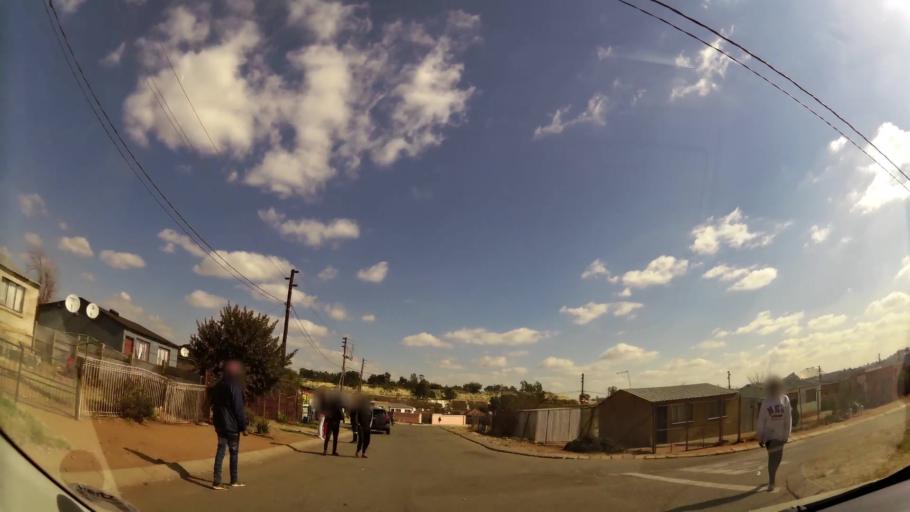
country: ZA
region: Gauteng
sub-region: West Rand District Municipality
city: Krugersdorp
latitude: -26.1429
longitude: 27.7829
